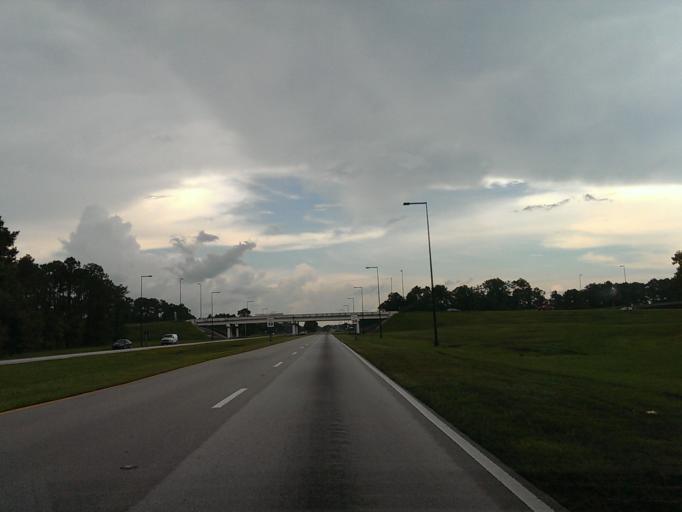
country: US
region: Florida
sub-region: Osceola County
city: Celebration
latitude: 28.3760
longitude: -81.5650
